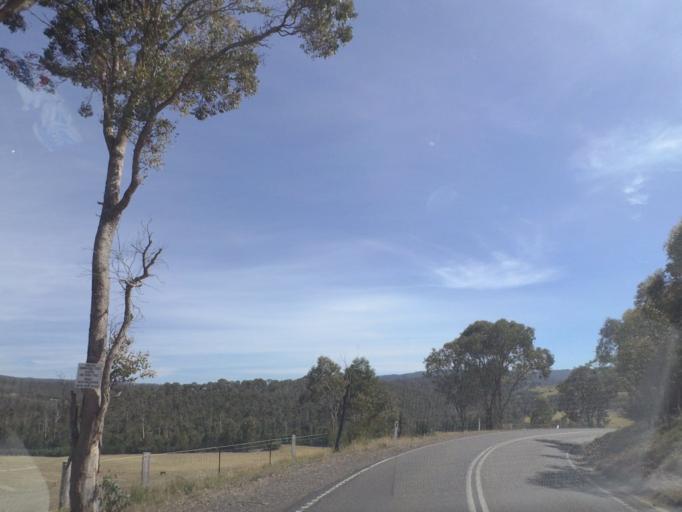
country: AU
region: Victoria
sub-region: Nillumbik
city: Saint Andrews
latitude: -37.5794
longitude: 145.2878
